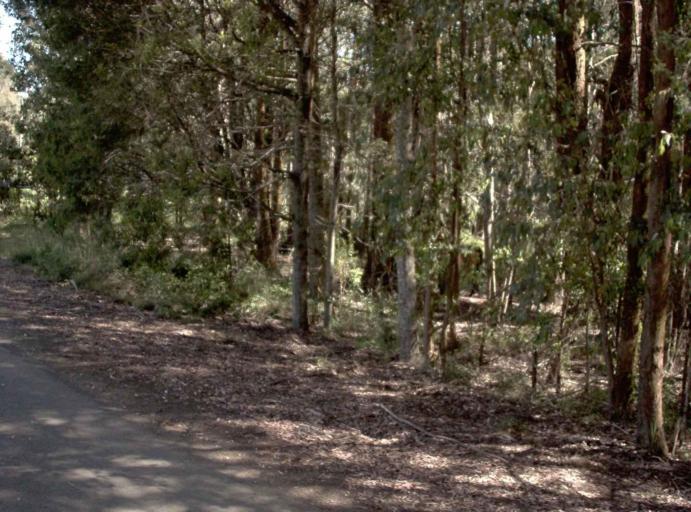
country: AU
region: New South Wales
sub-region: Bombala
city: Bombala
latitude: -37.2036
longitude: 148.7304
